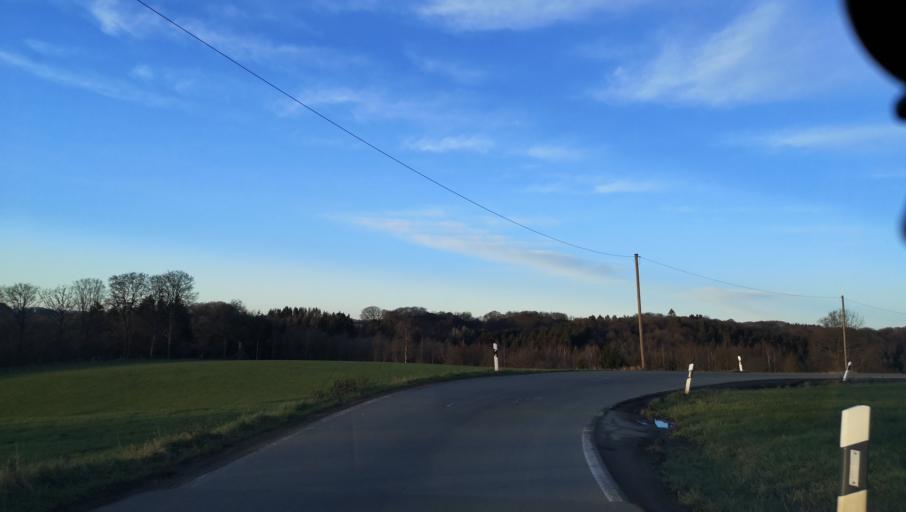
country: DE
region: North Rhine-Westphalia
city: Huckeswagen
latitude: 51.1607
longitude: 7.3349
